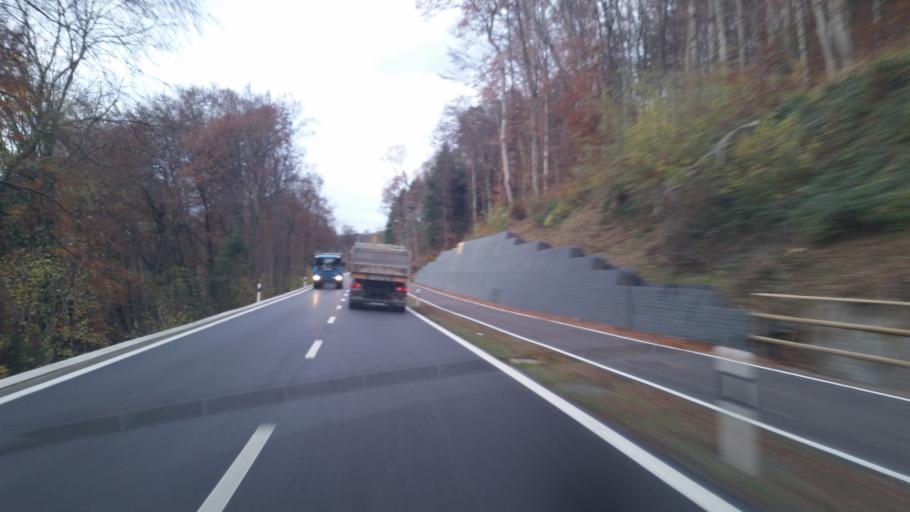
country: CH
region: Aargau
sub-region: Bezirk Baden
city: Kunten
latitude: 47.3783
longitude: 8.3322
